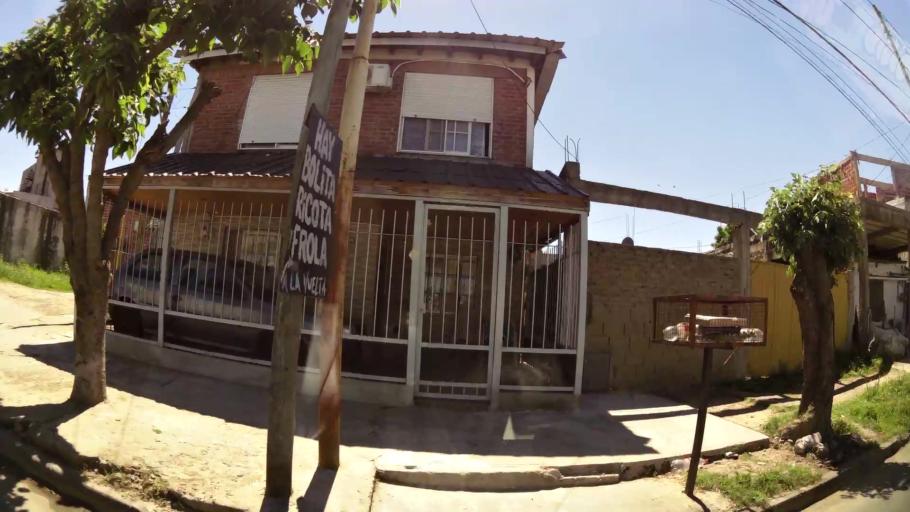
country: AR
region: Buenos Aires
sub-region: Partido de Lanus
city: Lanus
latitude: -34.7360
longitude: -58.3433
